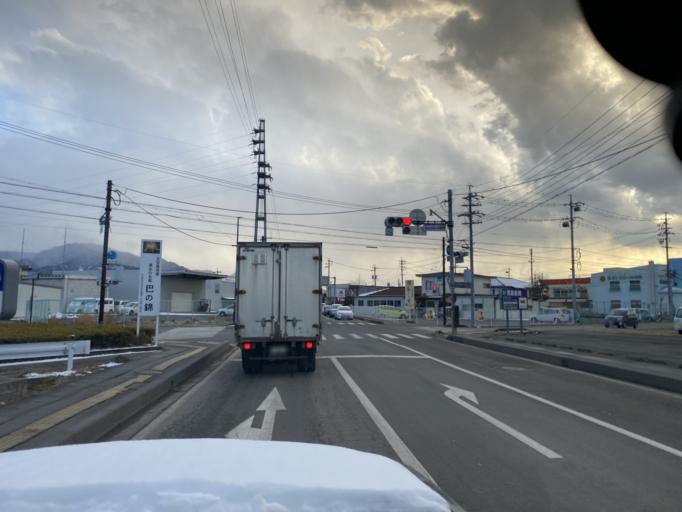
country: JP
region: Nagano
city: Nagano-shi
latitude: 36.6341
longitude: 138.2400
